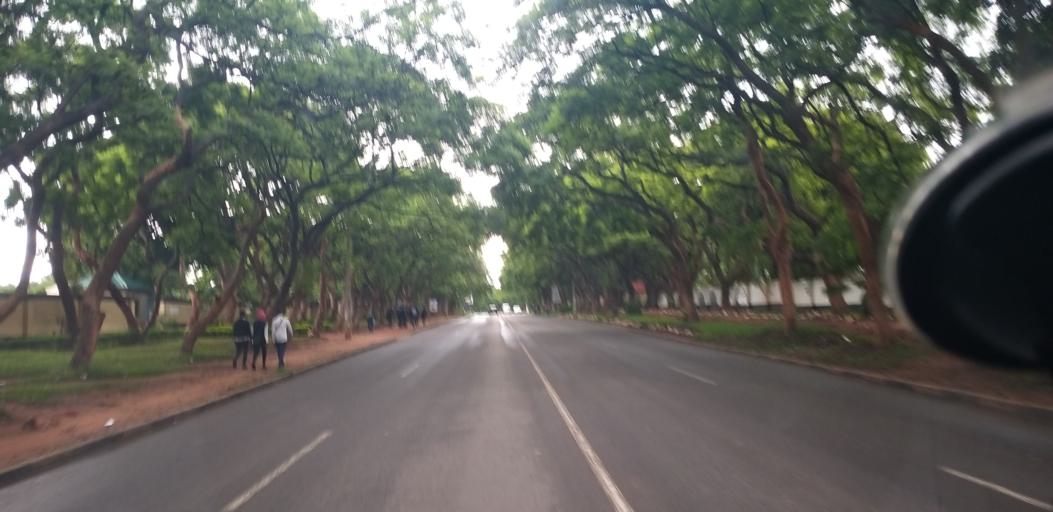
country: ZM
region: Lusaka
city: Lusaka
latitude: -15.4152
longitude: 28.3026
